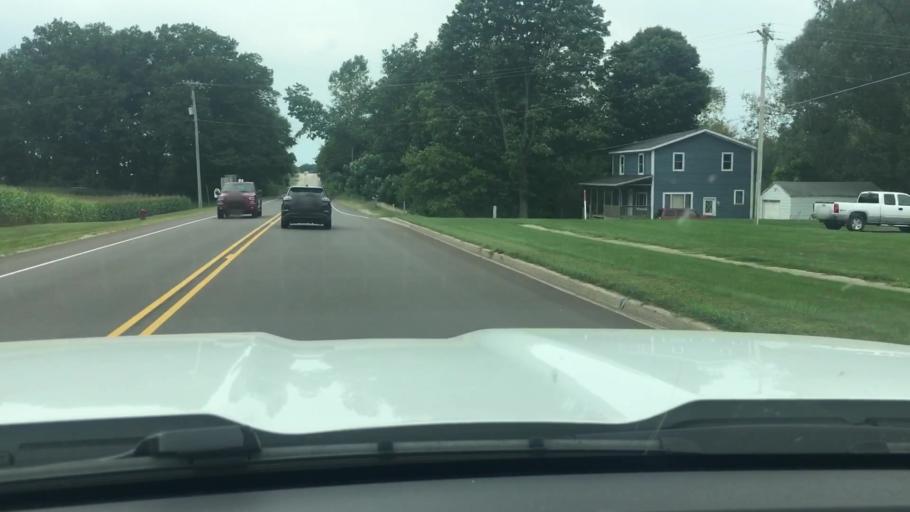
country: US
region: Michigan
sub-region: Allegan County
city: Otsego
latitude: 42.5372
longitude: -85.6498
